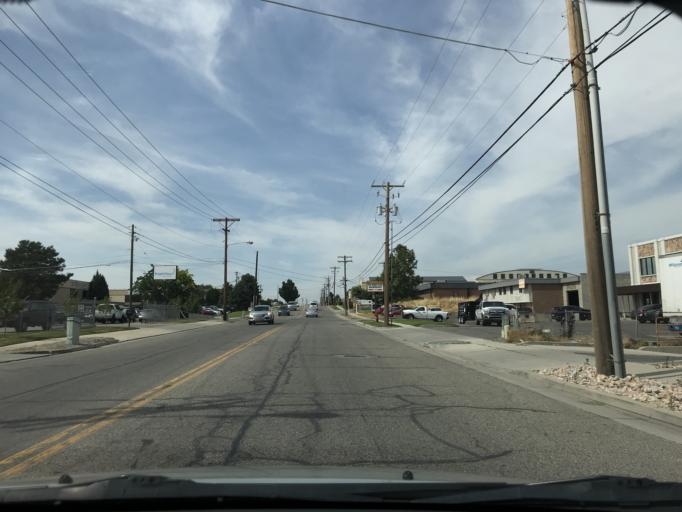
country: US
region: Utah
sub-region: Salt Lake County
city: Centerfield
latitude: 40.6820
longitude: -111.9055
